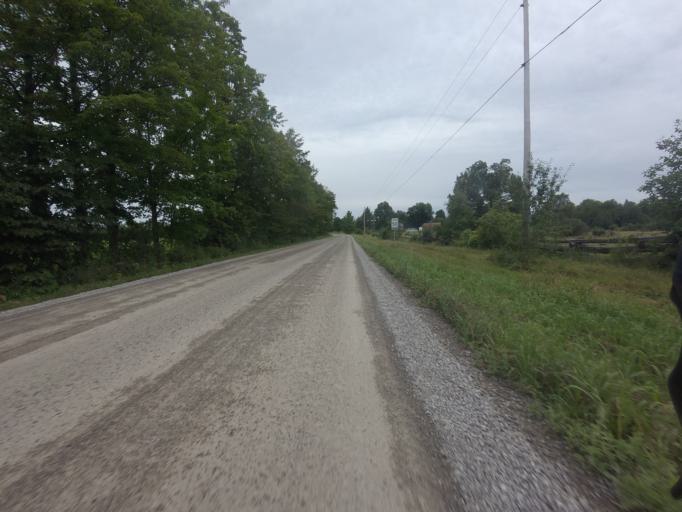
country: CA
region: Ontario
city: Carleton Place
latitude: 45.1465
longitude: -76.1734
